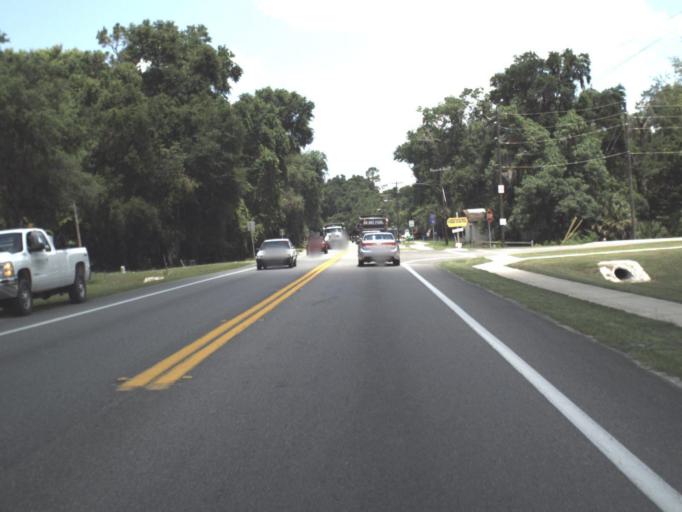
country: US
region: Florida
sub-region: Alachua County
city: High Springs
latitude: 29.9194
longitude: -82.7093
